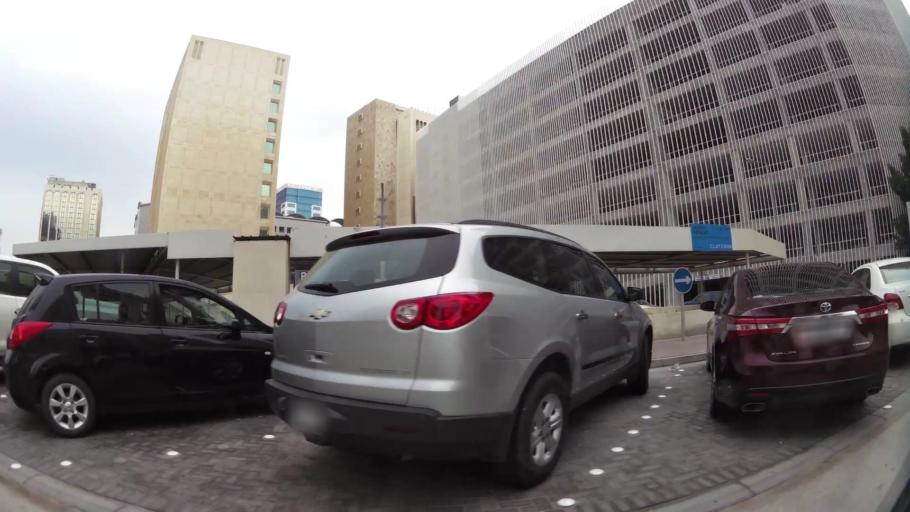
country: BH
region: Manama
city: Manama
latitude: 26.2401
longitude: 50.5891
